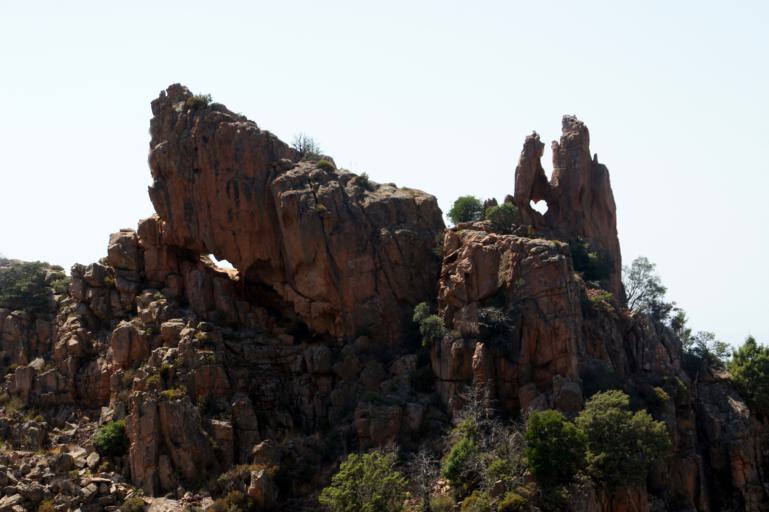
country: FR
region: Corsica
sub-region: Departement de la Corse-du-Sud
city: Cargese
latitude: 42.2434
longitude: 8.6541
